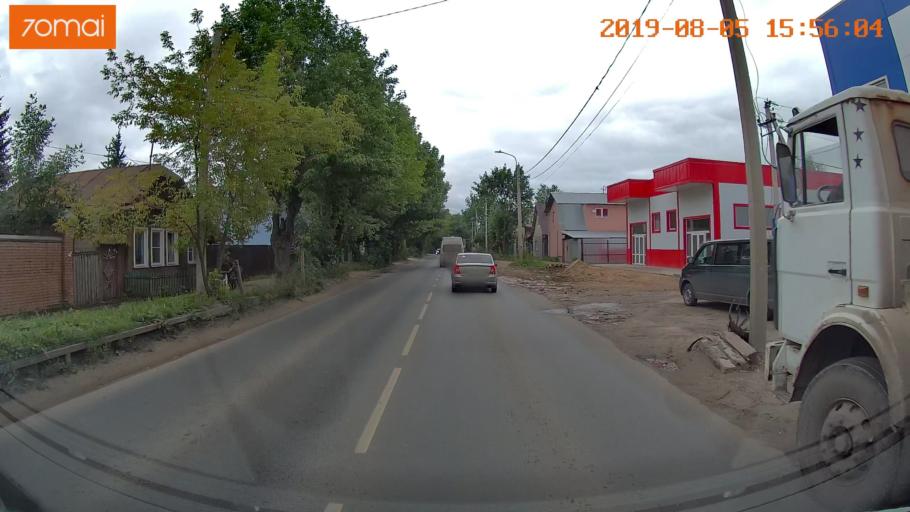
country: RU
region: Ivanovo
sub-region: Gorod Ivanovo
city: Ivanovo
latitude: 56.9943
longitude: 40.9521
